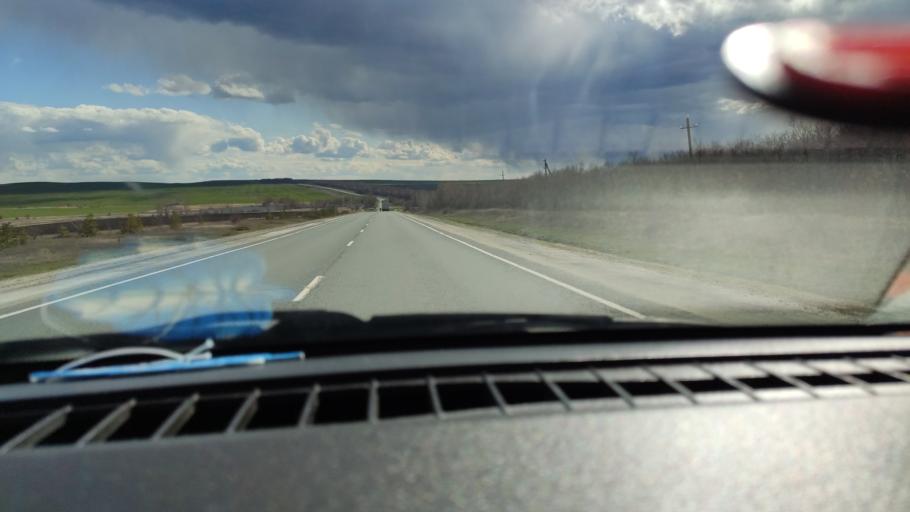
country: RU
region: Saratov
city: Alekseyevka
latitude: 52.2515
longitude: 47.9130
